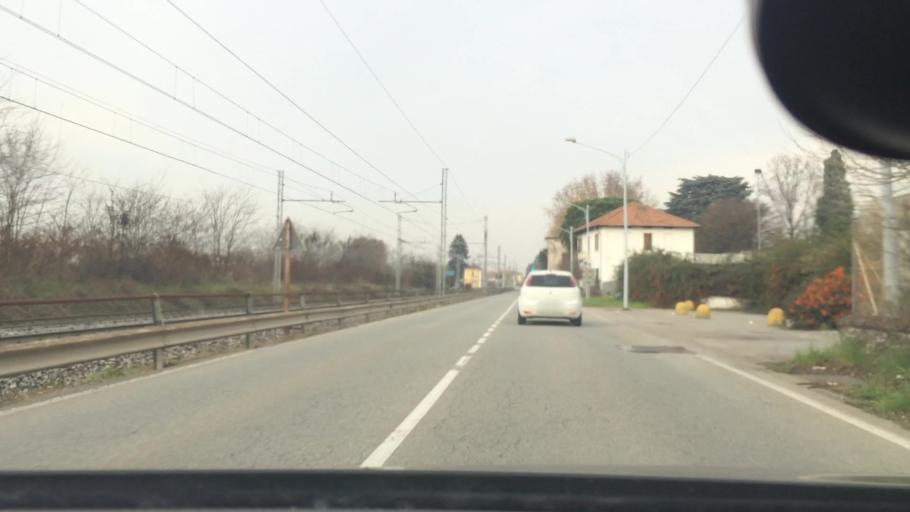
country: IT
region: Lombardy
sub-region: Provincia di Como
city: Manera
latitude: 45.6631
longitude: 9.0383
